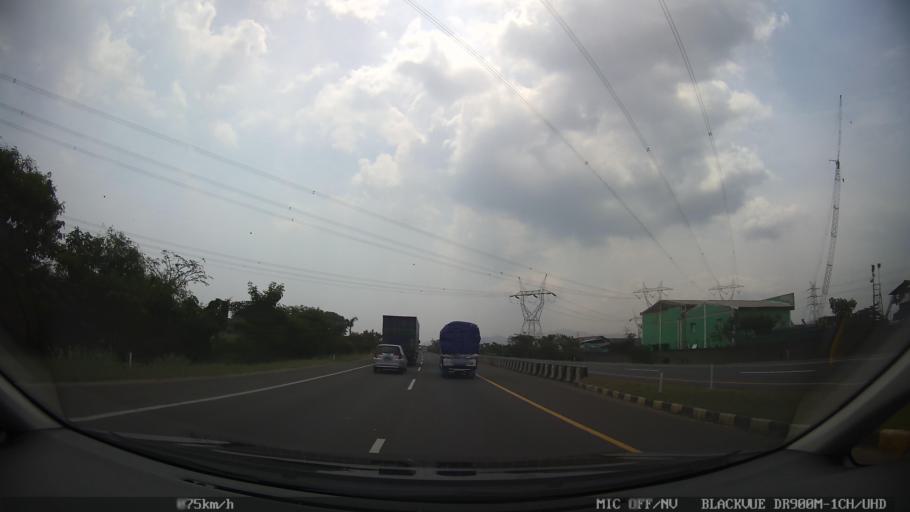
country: ID
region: Banten
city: Bojonegara
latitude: -6.0165
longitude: 106.0860
